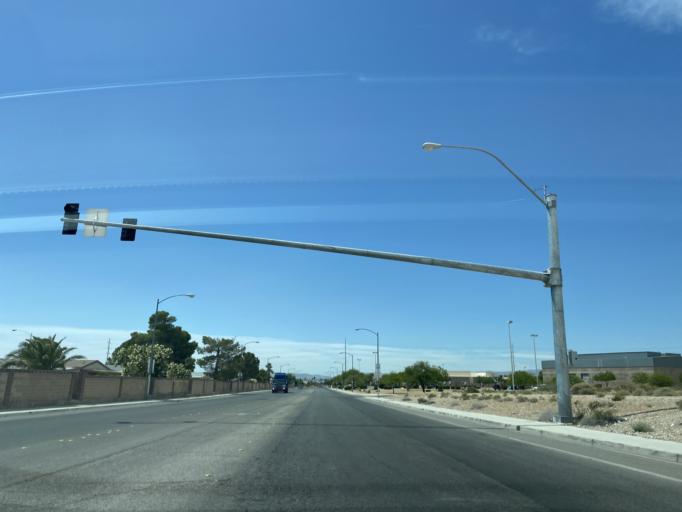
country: US
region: Nevada
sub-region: Clark County
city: Spring Valley
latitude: 36.1183
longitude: -115.2700
